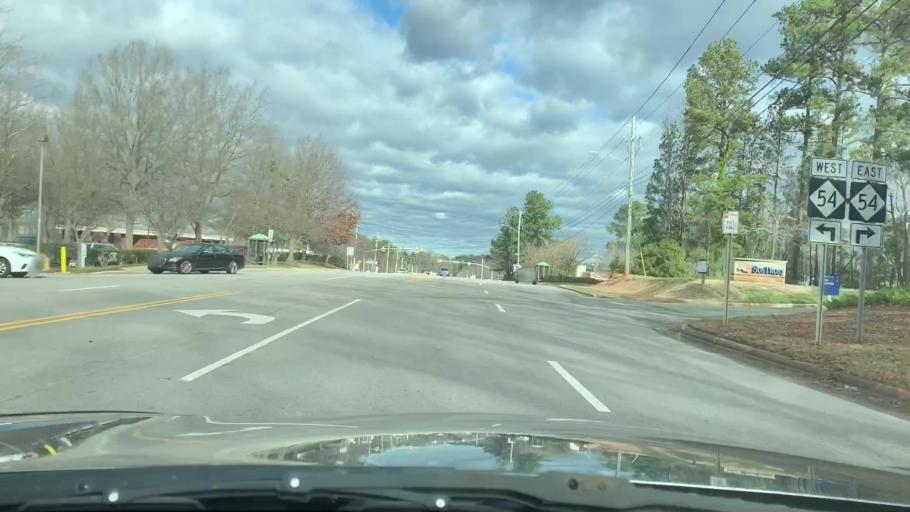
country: US
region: North Carolina
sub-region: Wake County
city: Cary
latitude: 35.8010
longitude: -78.7830
